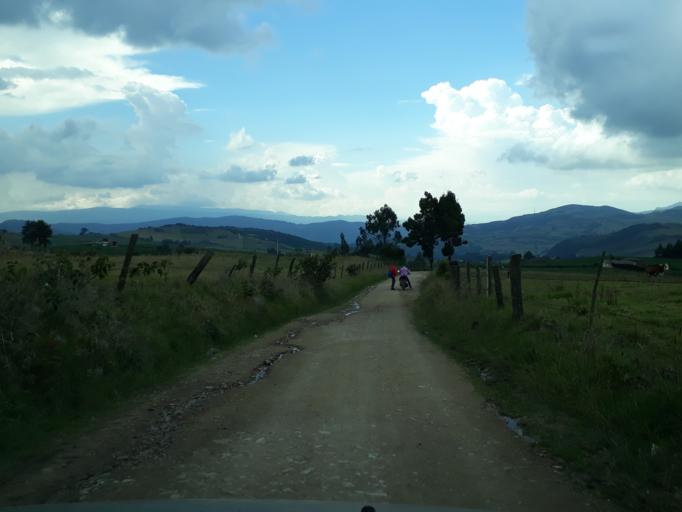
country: CO
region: Cundinamarca
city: Villapinzon
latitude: 5.2363
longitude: -73.6726
